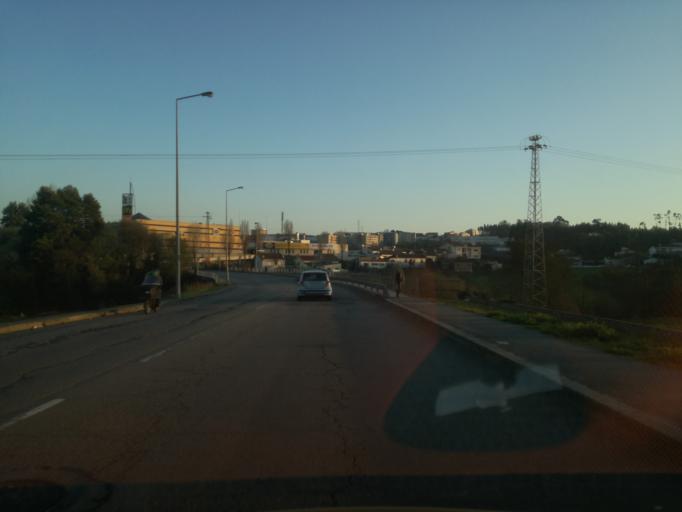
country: PT
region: Porto
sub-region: Valongo
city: Ermesinde
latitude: 41.2228
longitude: -8.5643
